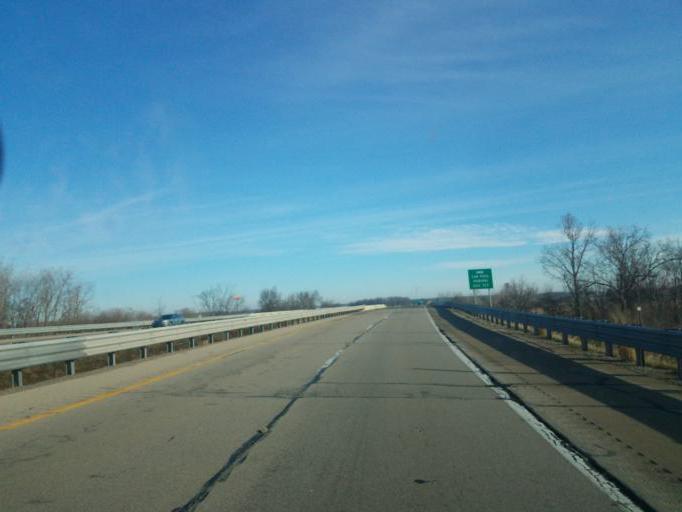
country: US
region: Michigan
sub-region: Gratiot County
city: Ithaca
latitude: 43.2861
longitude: -84.5821
